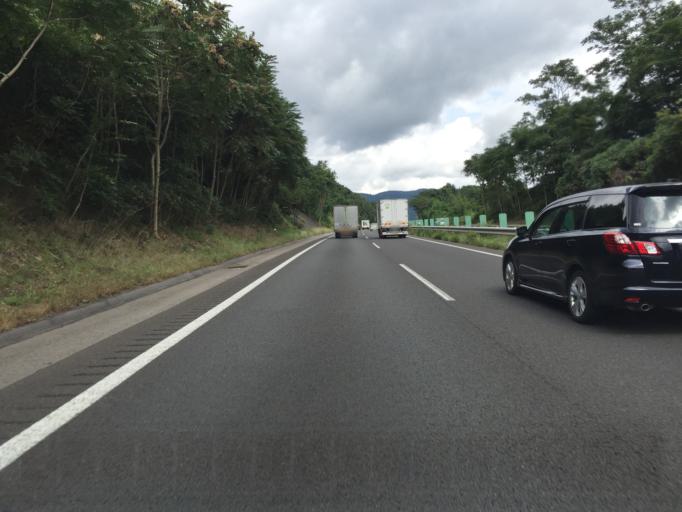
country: JP
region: Fukushima
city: Hobaramachi
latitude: 37.8594
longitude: 140.5146
